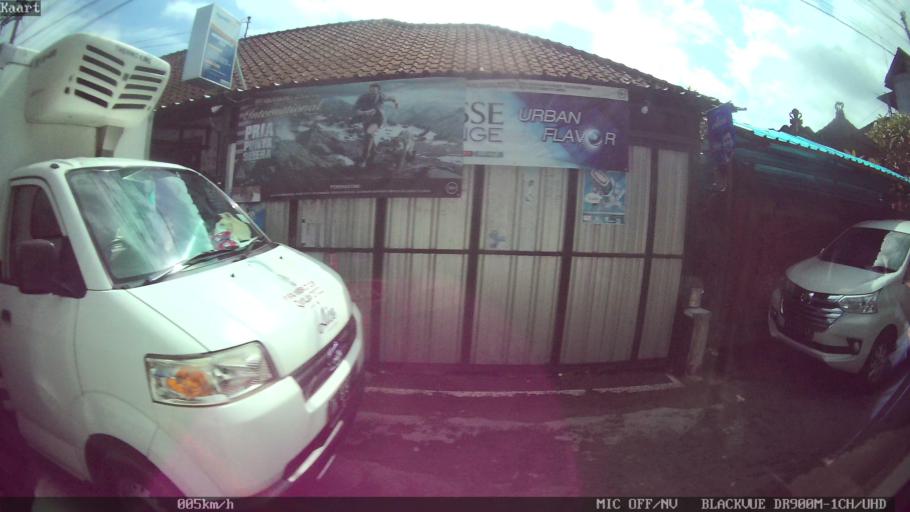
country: ID
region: Bali
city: Banjar Pesalakan
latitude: -8.5194
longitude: 115.3030
